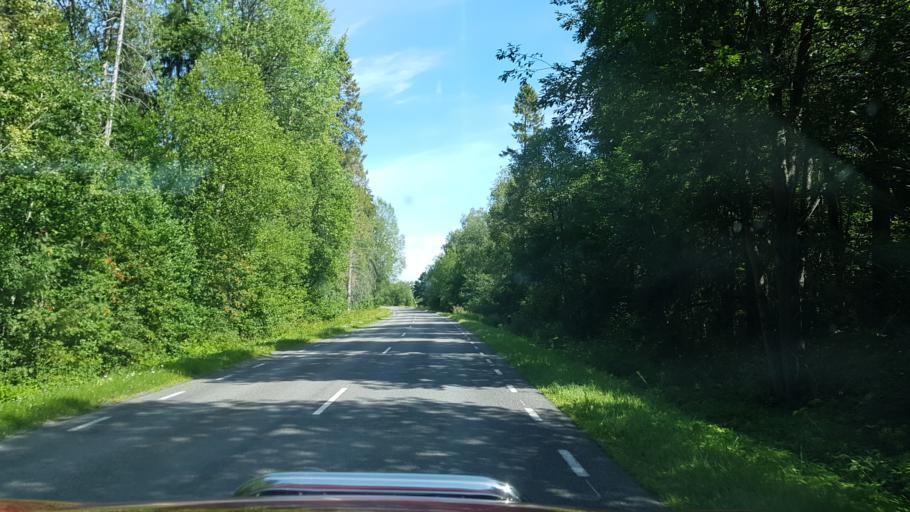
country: EE
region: Jaervamaa
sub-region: Jaerva-Jaani vald
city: Jarva-Jaani
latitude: 59.0580
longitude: 25.9239
